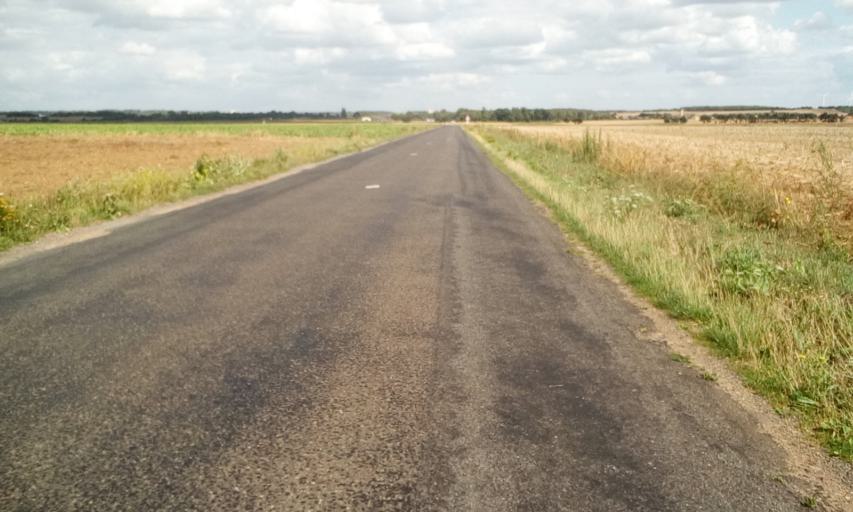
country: FR
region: Lower Normandy
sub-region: Departement du Calvados
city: Bellengreville
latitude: 49.0929
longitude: -0.2154
